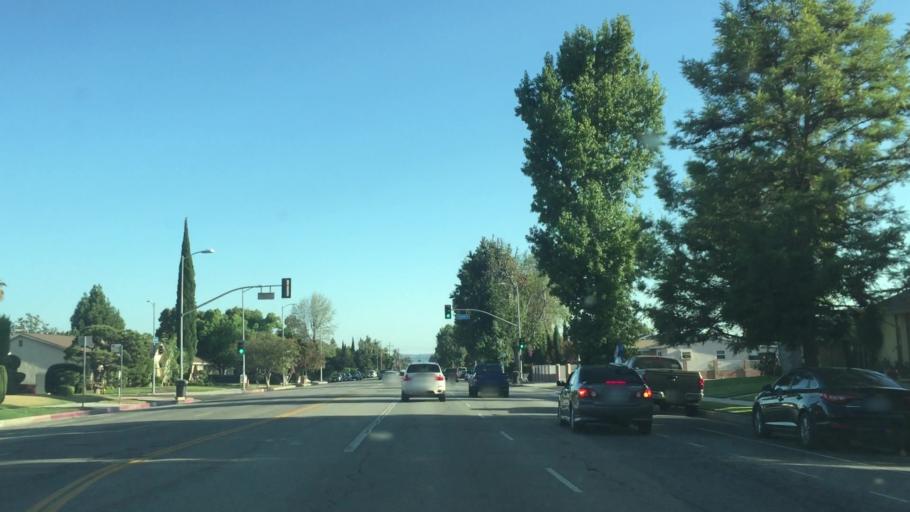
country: US
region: California
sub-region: Los Angeles County
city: Northridge
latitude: 34.2399
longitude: -118.4851
